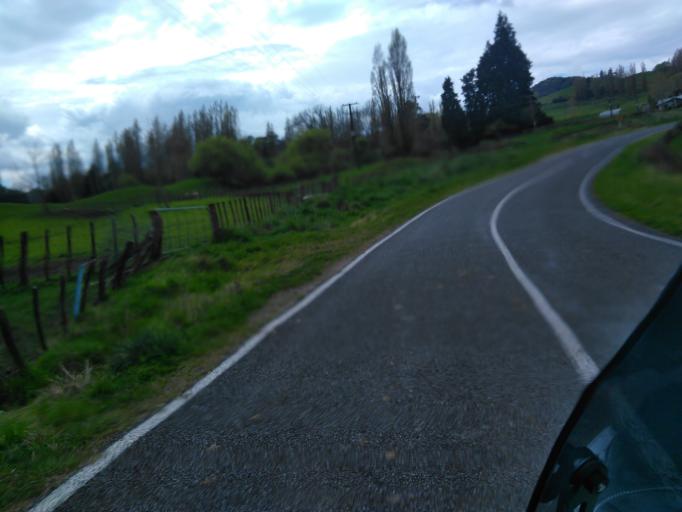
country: NZ
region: Hawke's Bay
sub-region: Wairoa District
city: Wairoa
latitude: -38.7745
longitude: 177.5639
